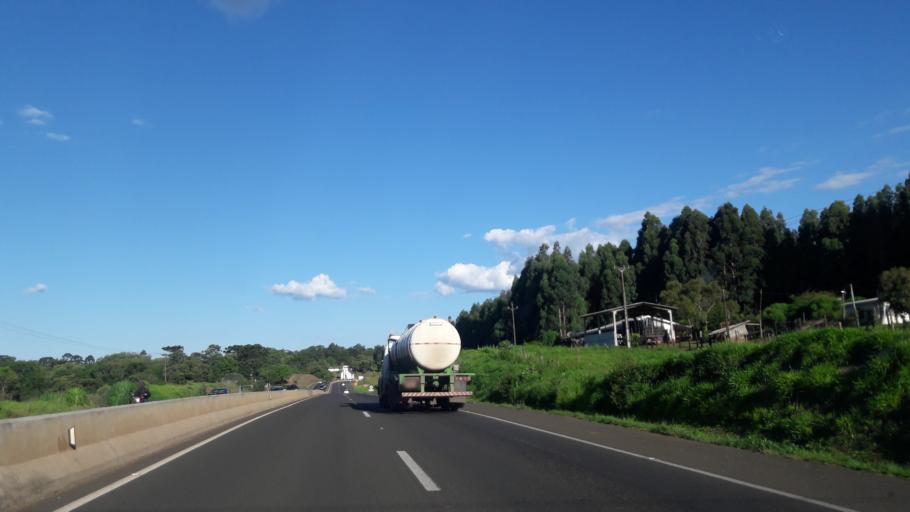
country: BR
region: Parana
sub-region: Guarapuava
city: Guarapuava
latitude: -25.3444
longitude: -51.3983
